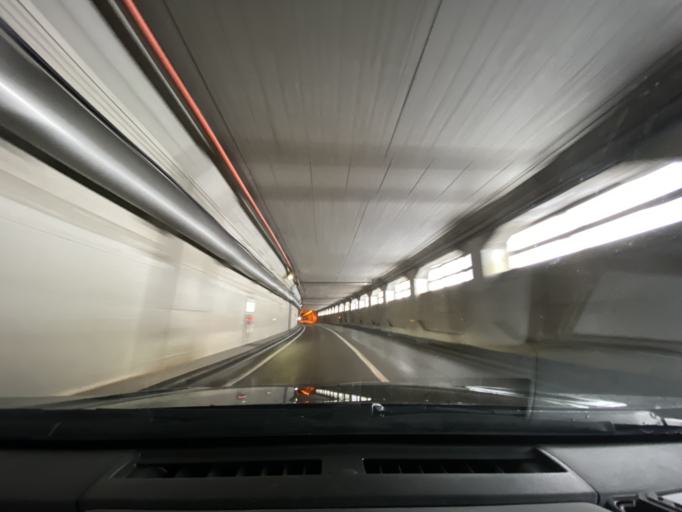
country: JP
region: Hokkaido
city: Rumoi
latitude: 43.7971
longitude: 141.3771
